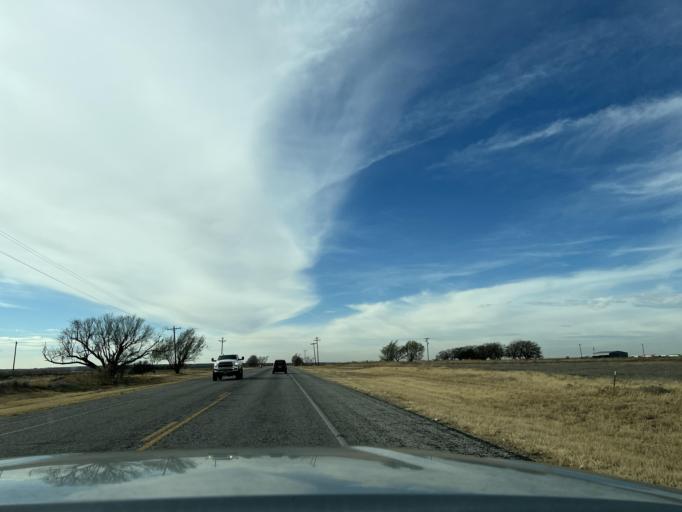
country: US
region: Texas
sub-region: Fisher County
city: Roby
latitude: 32.7589
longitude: -100.2866
